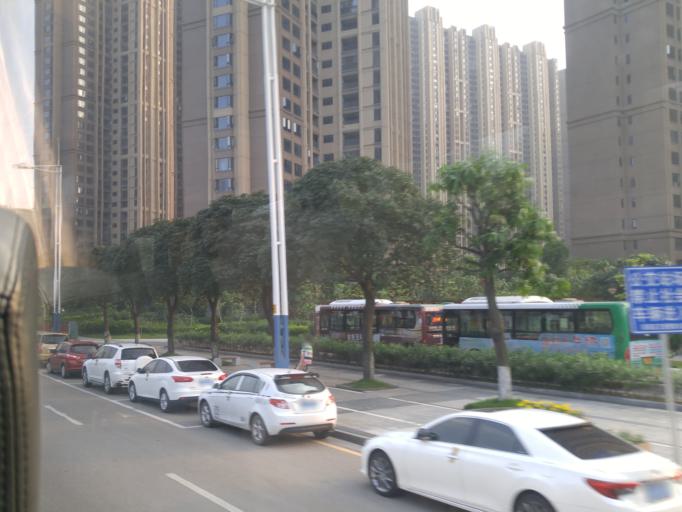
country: CN
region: Guangdong
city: Foshan
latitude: 23.0683
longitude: 113.1405
